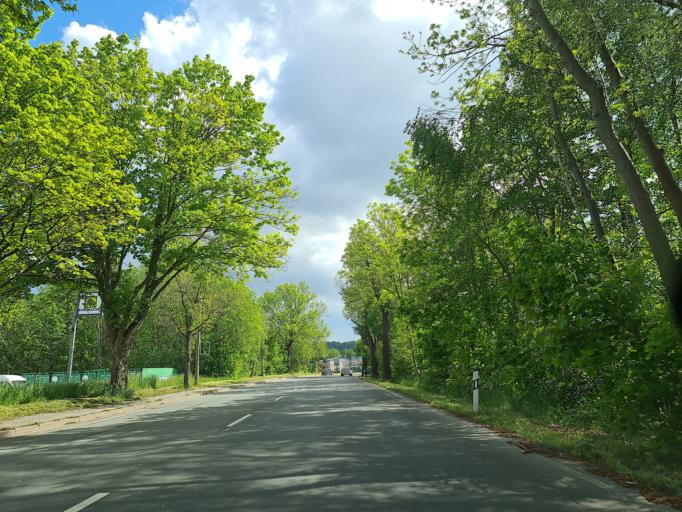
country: DE
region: Saxony
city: Wilkau-Hasslau
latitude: 50.6913
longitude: 12.4959
